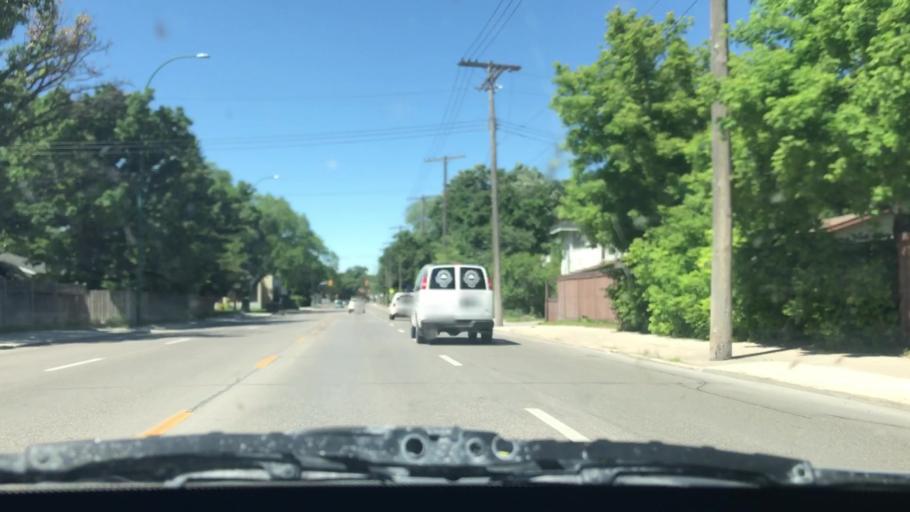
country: CA
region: Manitoba
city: Winnipeg
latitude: 49.8716
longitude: -97.1642
